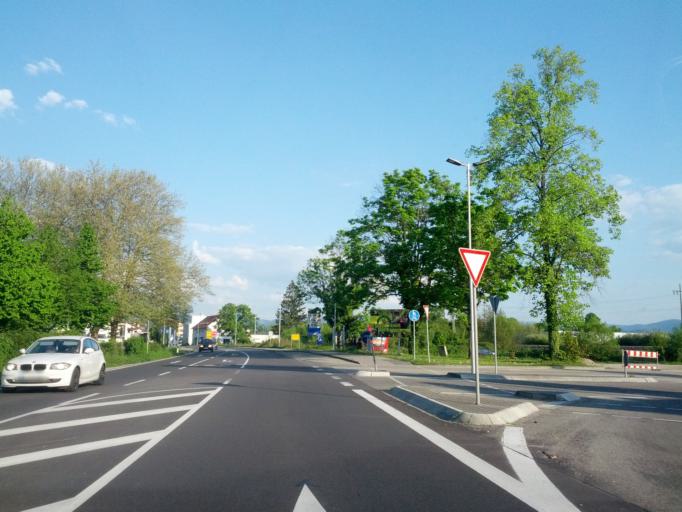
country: DE
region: Baden-Wuerttemberg
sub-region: Freiburg Region
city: Teningen
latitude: 48.1266
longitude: 7.8322
